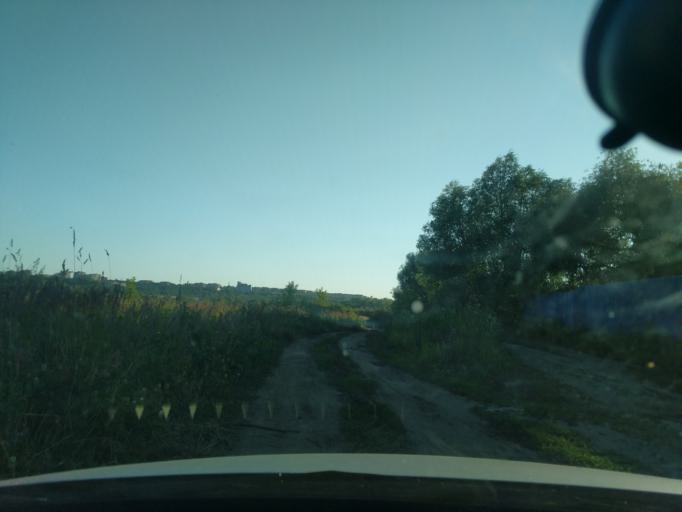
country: RU
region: Moskovskaya
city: Pushchino
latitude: 54.8483
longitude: 37.6415
